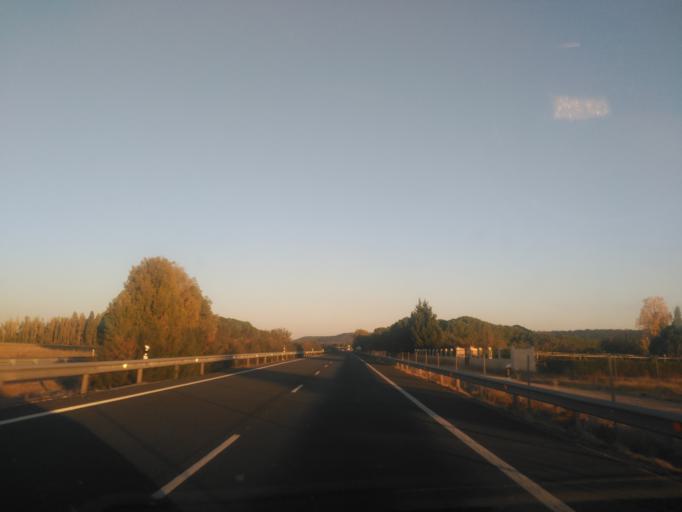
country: ES
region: Castille and Leon
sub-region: Provincia de Valladolid
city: Tudela de Duero
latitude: 41.5912
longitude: -4.5697
